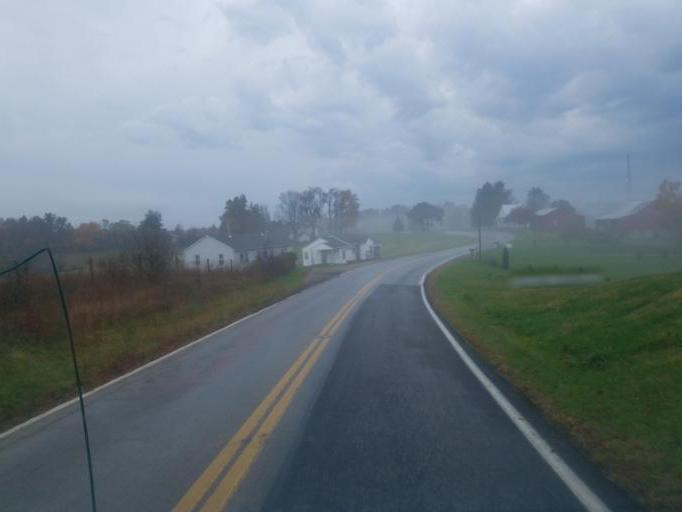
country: US
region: Ohio
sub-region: Morgan County
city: McConnelsville
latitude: 39.4908
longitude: -81.8757
